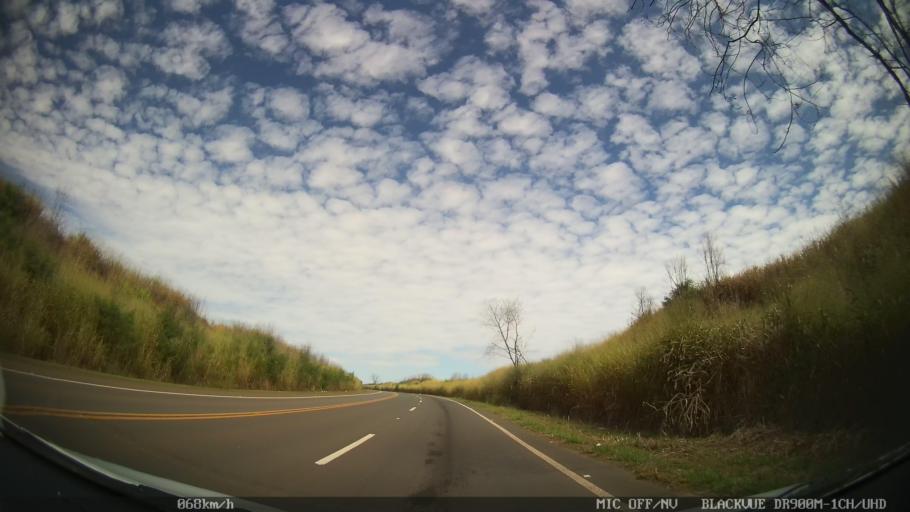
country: BR
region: Sao Paulo
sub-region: Santa Barbara D'Oeste
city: Santa Barbara d'Oeste
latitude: -22.7195
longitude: -47.4267
